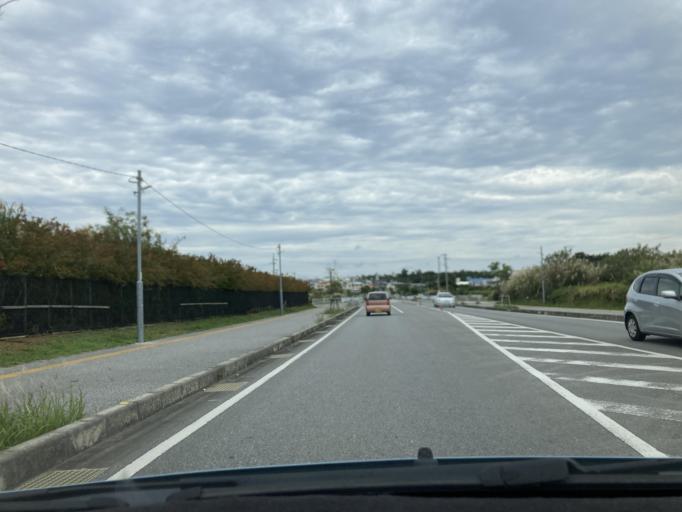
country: JP
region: Okinawa
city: Ishikawa
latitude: 26.3980
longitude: 127.7405
